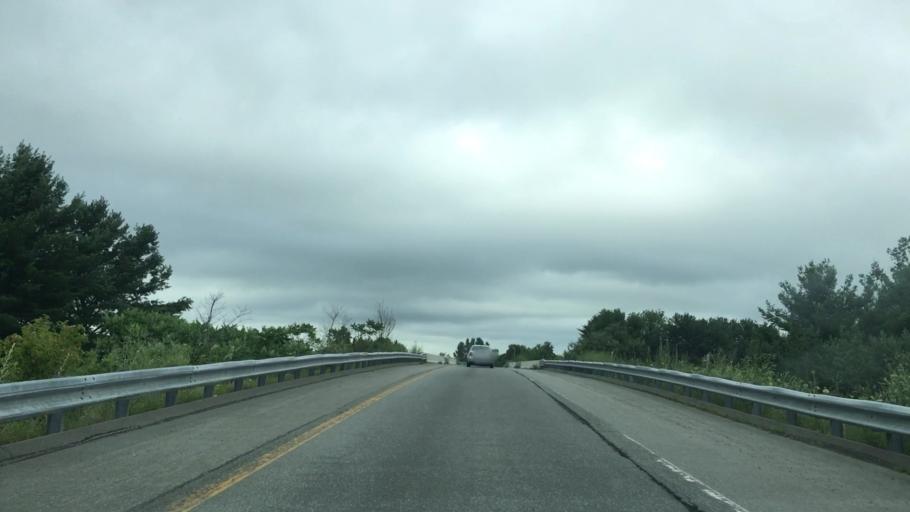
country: US
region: Maine
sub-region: Penobscot County
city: Brewer
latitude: 44.8245
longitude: -68.7540
